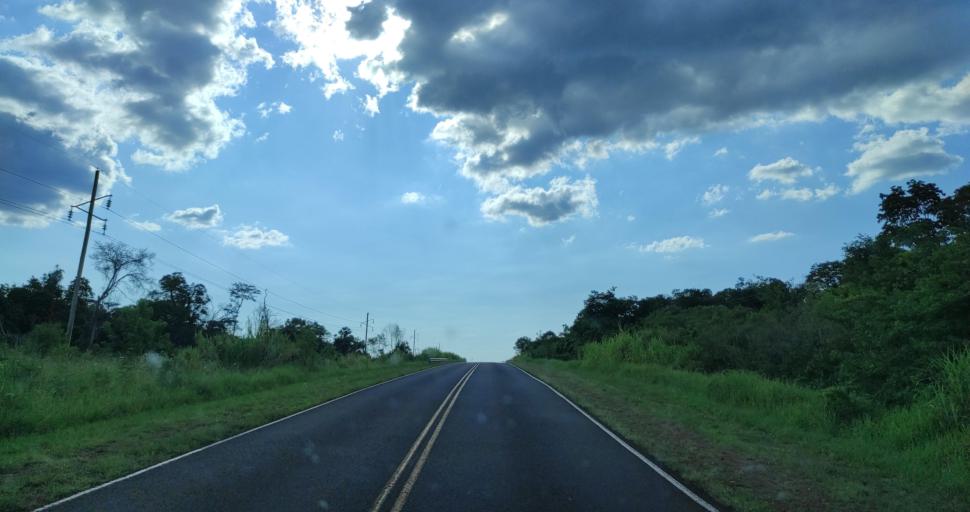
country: AR
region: Misiones
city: San Vicente
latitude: -26.3512
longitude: -54.1893
